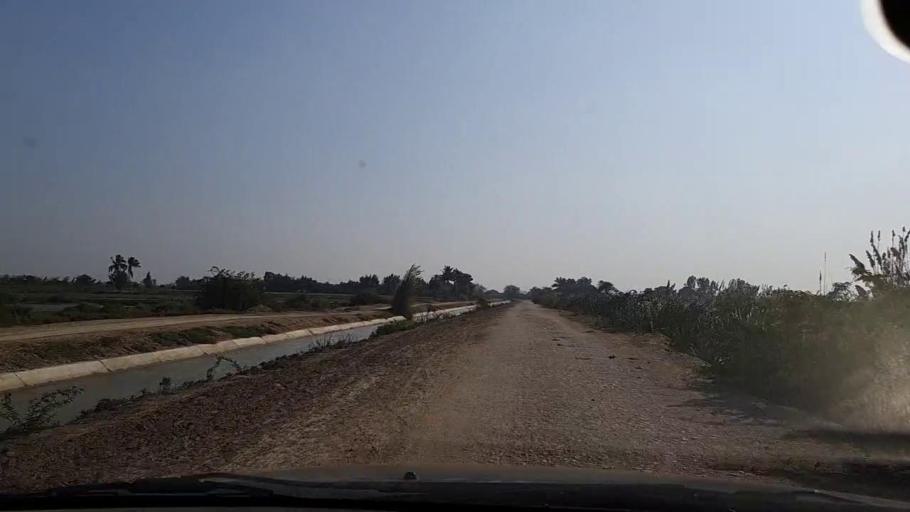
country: PK
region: Sindh
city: Mirpur Sakro
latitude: 24.3160
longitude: 67.7028
